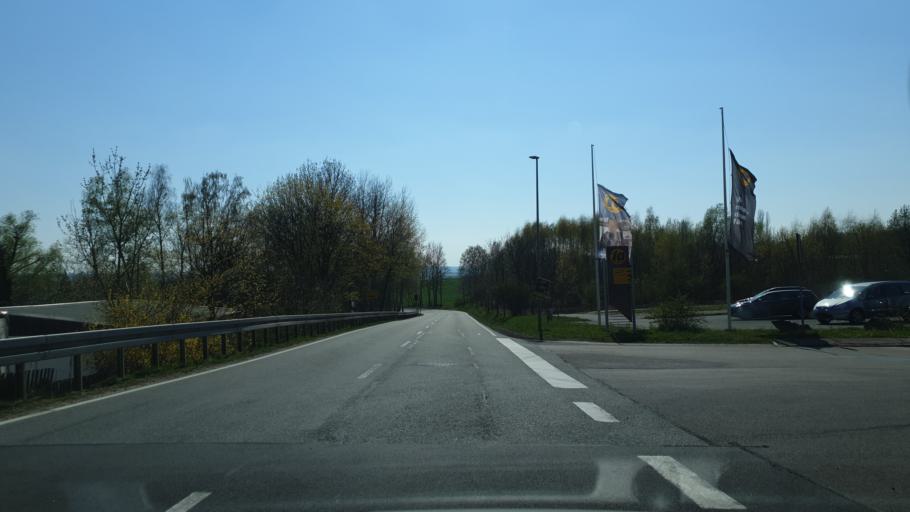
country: DE
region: Saxony
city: Kirchberg
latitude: 50.8023
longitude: 12.7586
